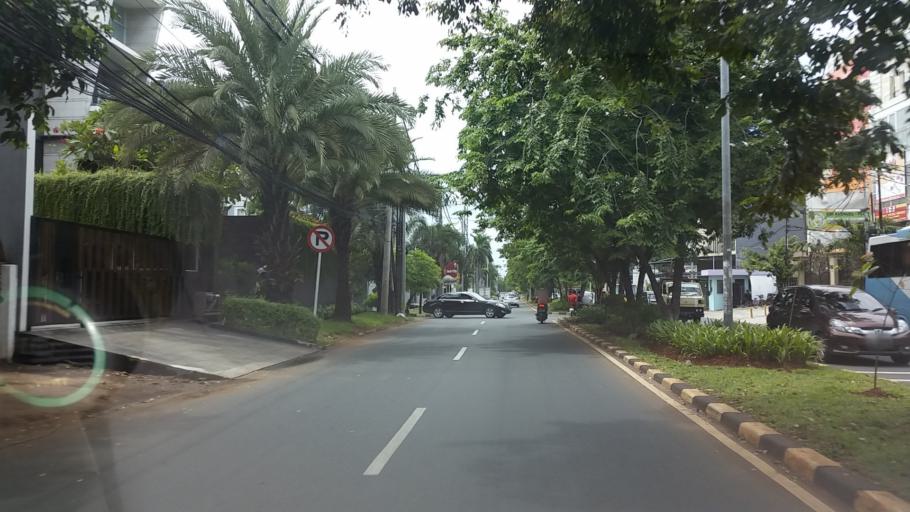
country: ID
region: Jakarta Raya
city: Jakarta
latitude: -6.1122
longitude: 106.7944
